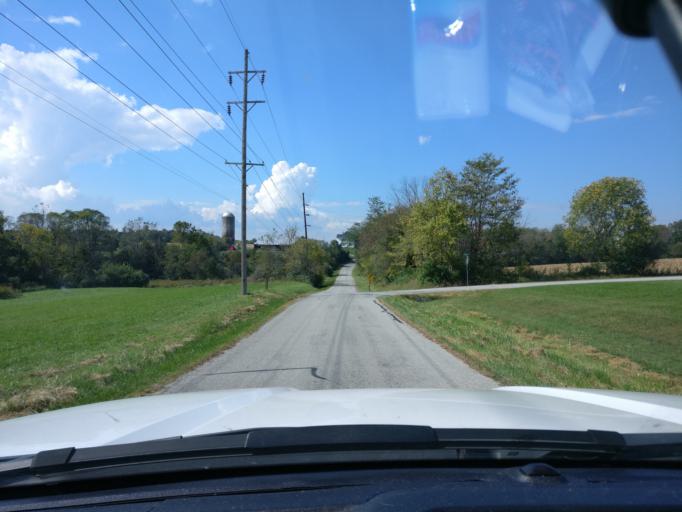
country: US
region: Ohio
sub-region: Clinton County
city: Wilmington
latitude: 39.4625
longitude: -83.9530
